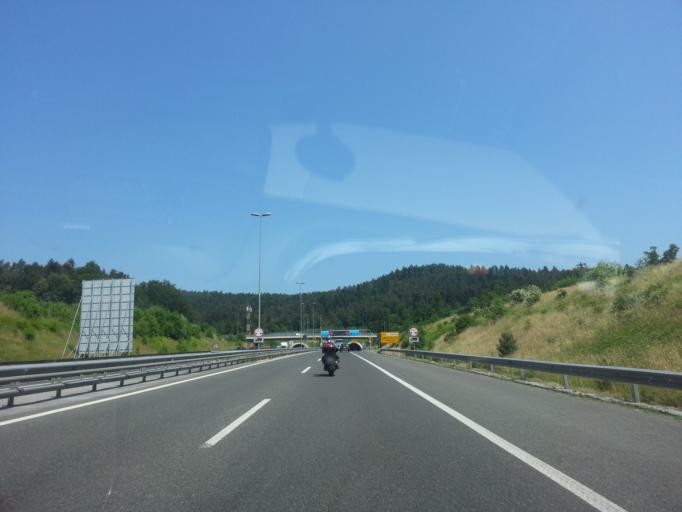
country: SI
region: Ljubljana
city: Ljubljana
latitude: 46.0840
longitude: 14.4607
